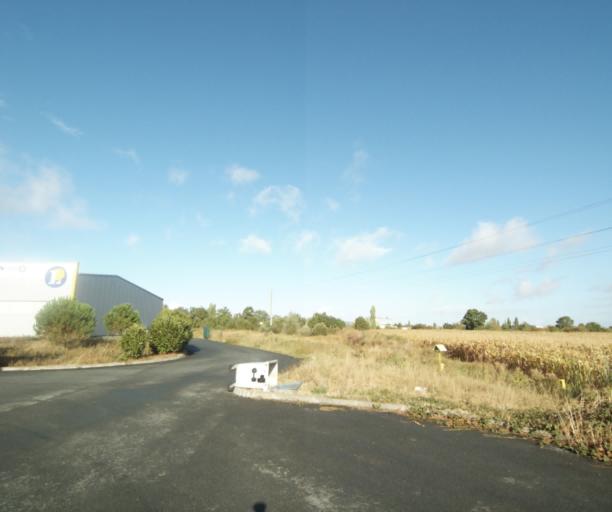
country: FR
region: Poitou-Charentes
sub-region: Departement de la Charente-Maritime
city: Tonnay-Charente
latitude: 45.9523
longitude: -0.9313
